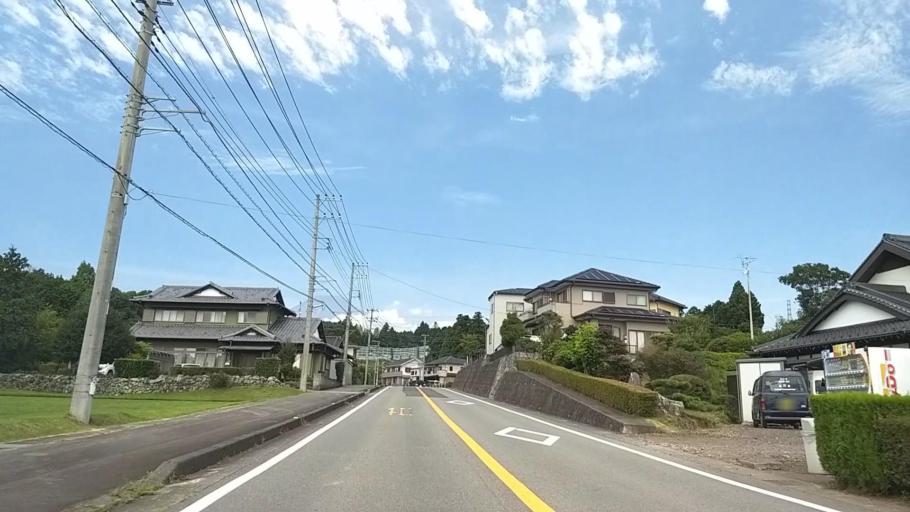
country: JP
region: Shizuoka
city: Gotemba
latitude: 35.2197
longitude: 138.8909
